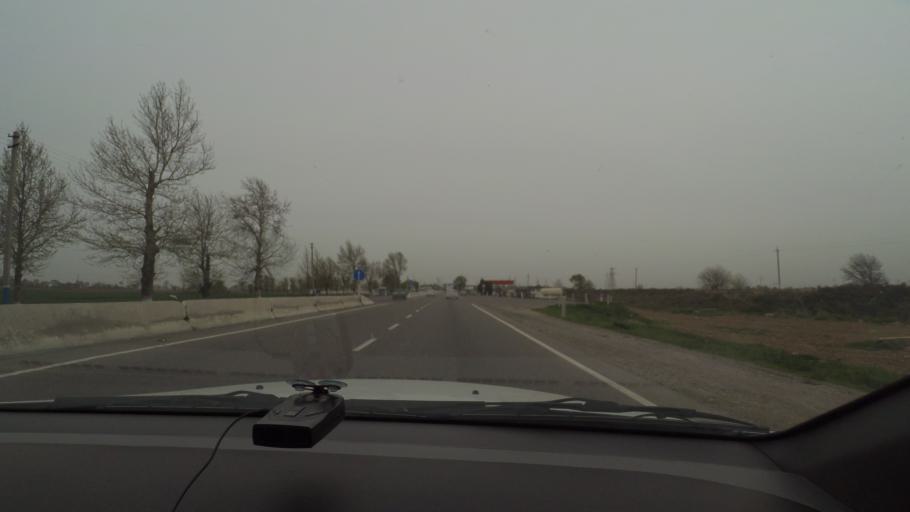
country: KZ
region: Ongtustik Qazaqstan
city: Myrzakent
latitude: 40.5574
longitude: 68.3674
